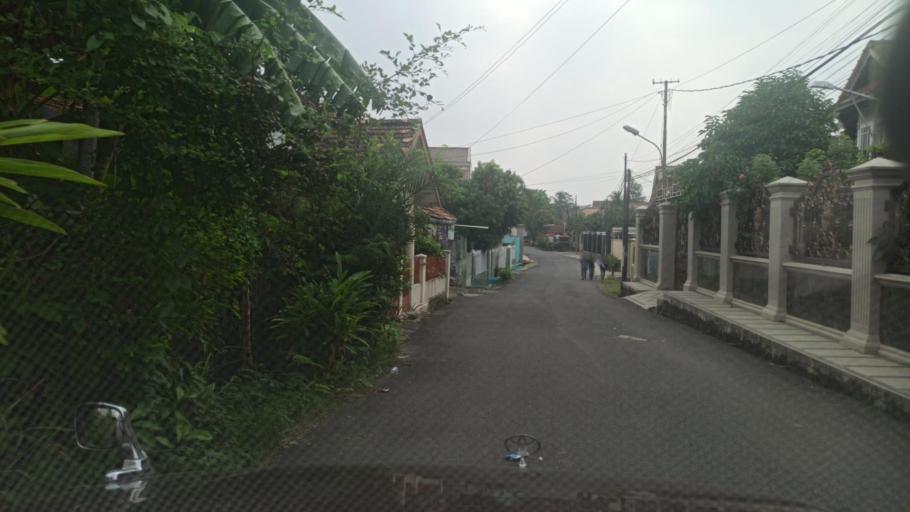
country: ID
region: South Sumatra
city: Plaju
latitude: -2.9920
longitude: 104.7425
